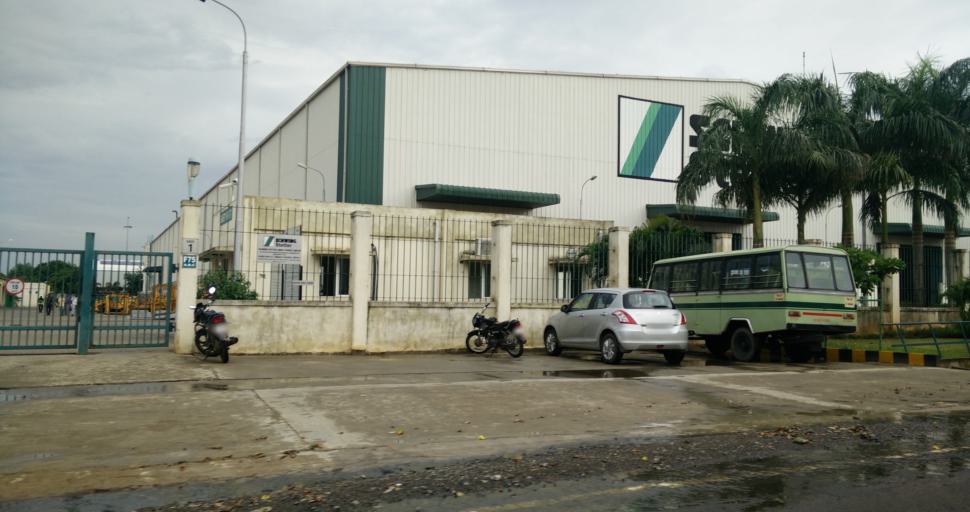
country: IN
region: Tamil Nadu
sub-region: Kancheepuram
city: Nandambakkam
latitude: 12.9996
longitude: 80.0251
